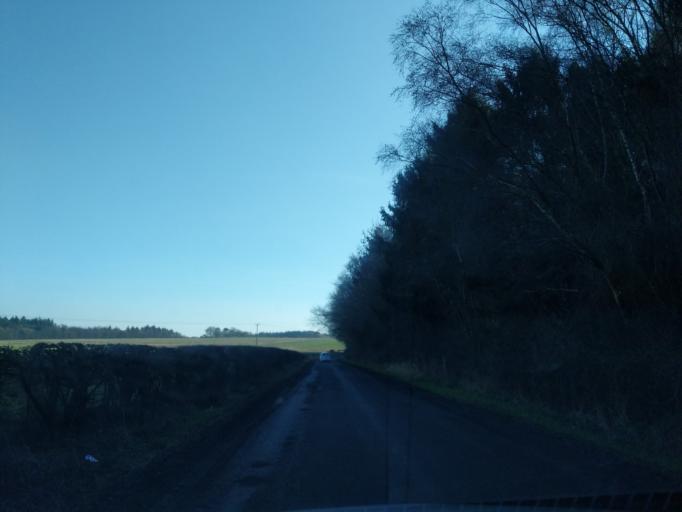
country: GB
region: Scotland
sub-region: South Lanarkshire
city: Carluke
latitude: 55.6925
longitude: -3.8415
